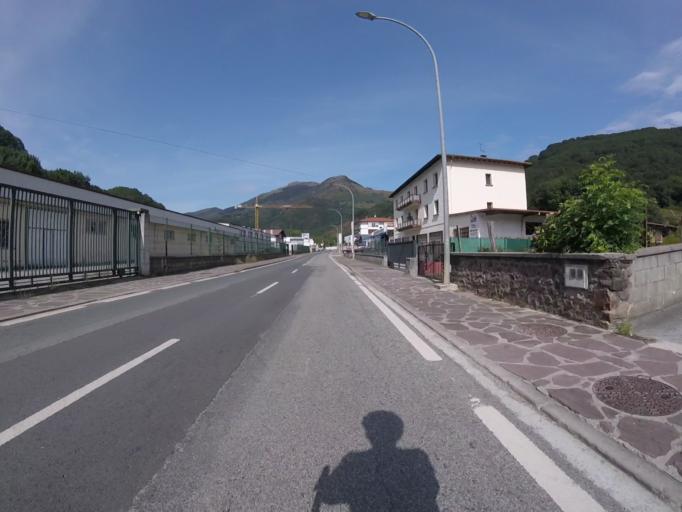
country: ES
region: Navarre
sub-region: Provincia de Navarra
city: Elgorriaga
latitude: 43.1345
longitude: -1.6774
